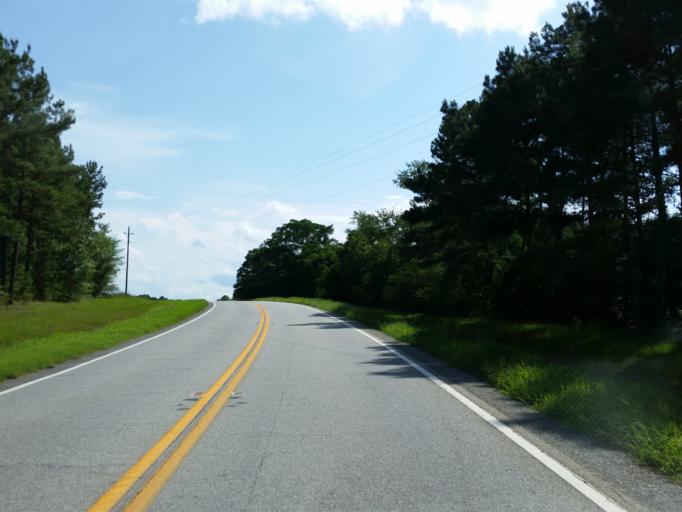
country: US
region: Georgia
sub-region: Turner County
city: Ashburn
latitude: 31.6898
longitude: -83.7141
